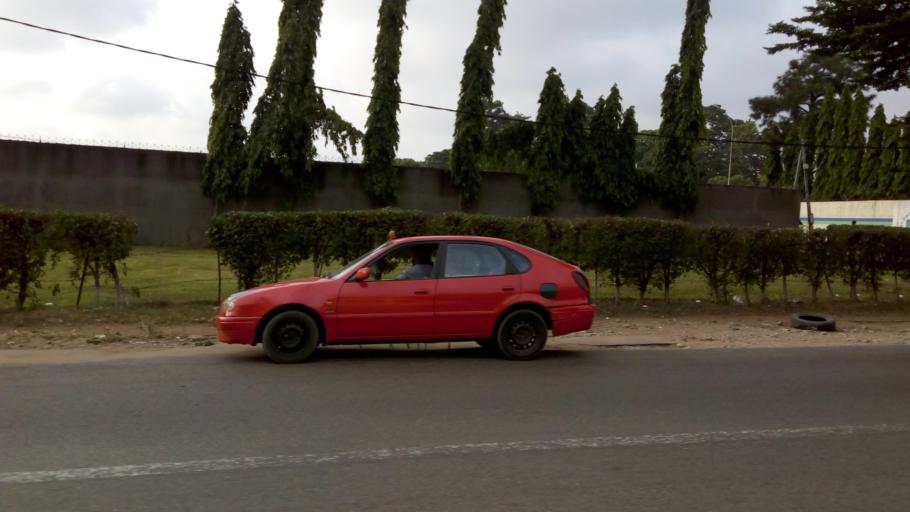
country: CI
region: Lagunes
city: Abidjan
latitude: 5.3486
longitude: -3.9994
